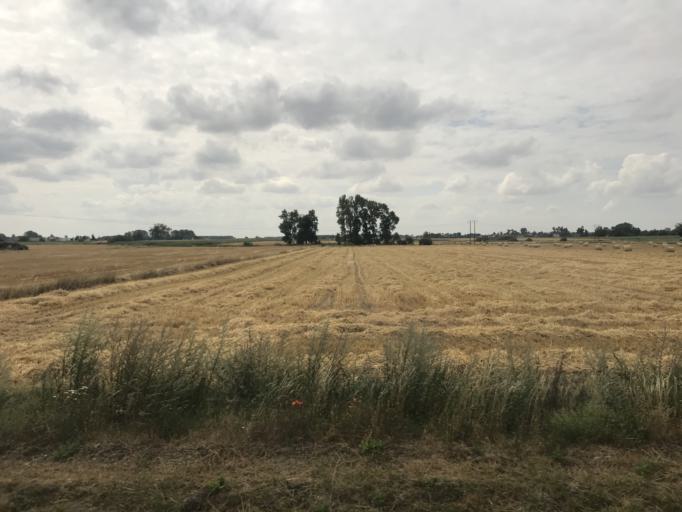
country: PL
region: Greater Poland Voivodeship
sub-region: Powiat gnieznienski
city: Niechanowo
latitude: 52.5341
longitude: 17.6772
